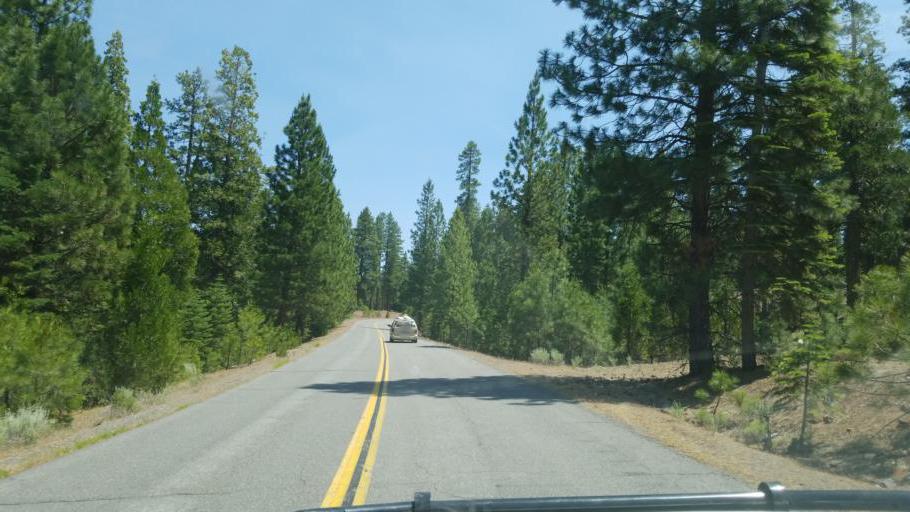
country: US
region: California
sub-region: Lassen County
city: Susanville
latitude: 40.5518
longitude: -120.8199
